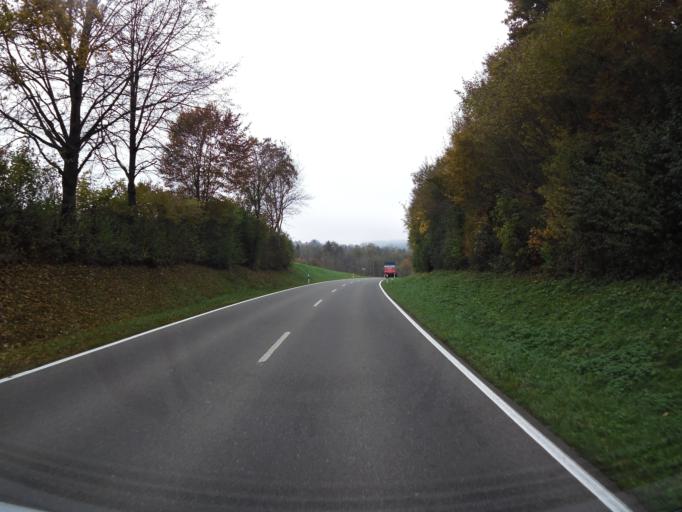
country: DE
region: Baden-Wuerttemberg
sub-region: Freiburg Region
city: Ohningen
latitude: 47.6795
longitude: 8.8901
